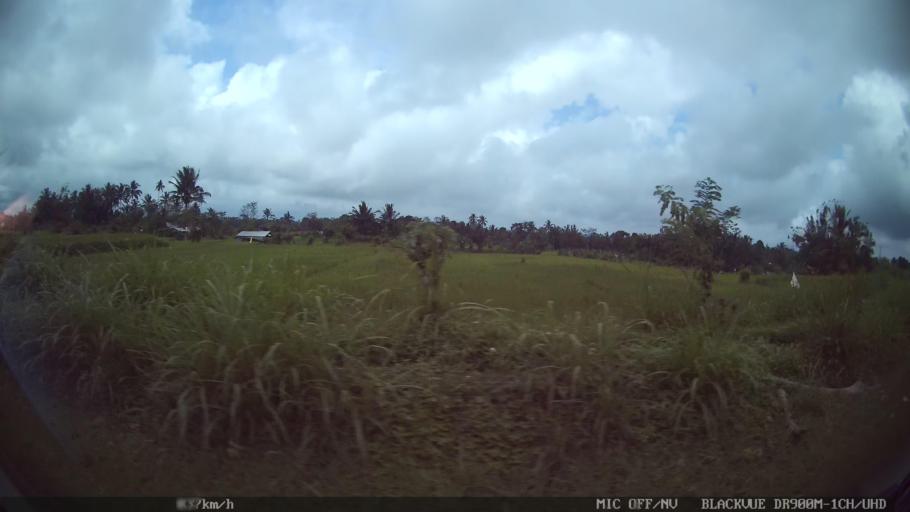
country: ID
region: Bali
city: Pemijian
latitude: -8.4347
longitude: 115.2261
